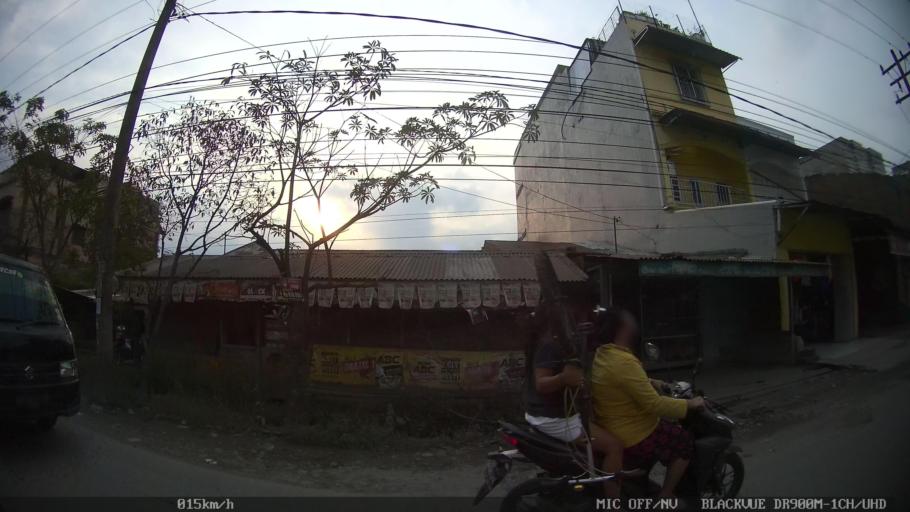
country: ID
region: North Sumatra
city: Sunggal
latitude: 3.5992
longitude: 98.6026
